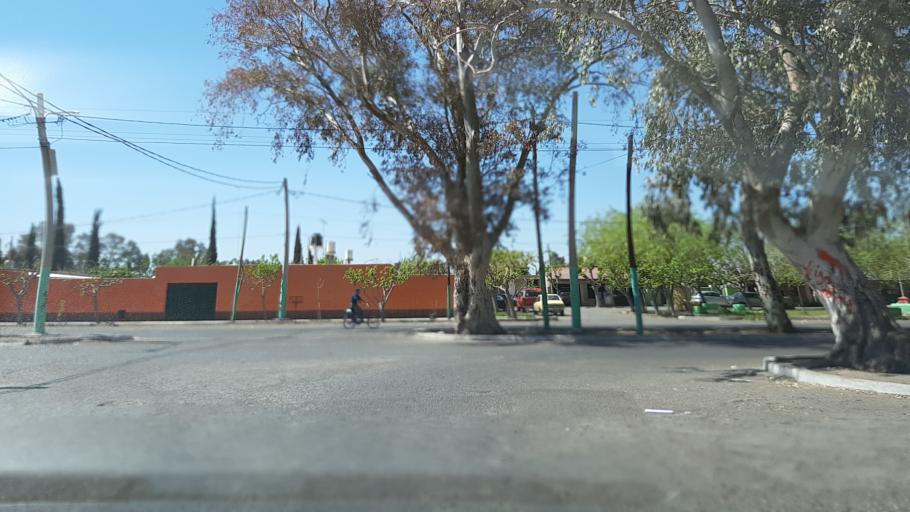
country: AR
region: San Juan
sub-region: Departamento de Rivadavia
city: Rivadavia
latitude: -31.5220
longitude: -68.6254
